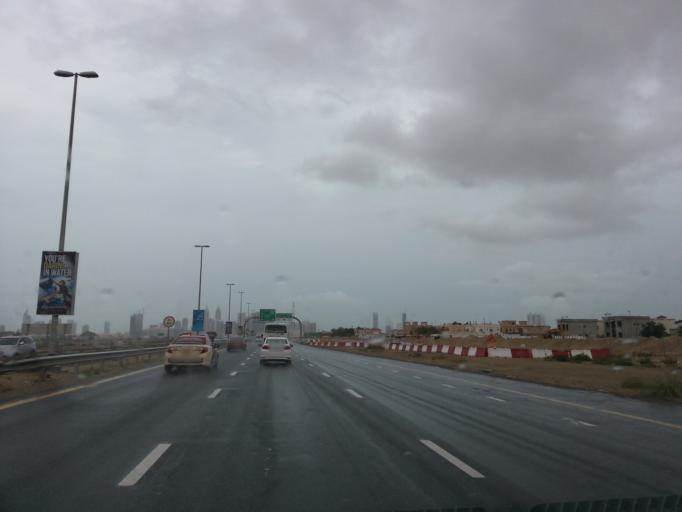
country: AE
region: Dubai
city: Dubai
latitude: 25.0793
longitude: 55.2071
